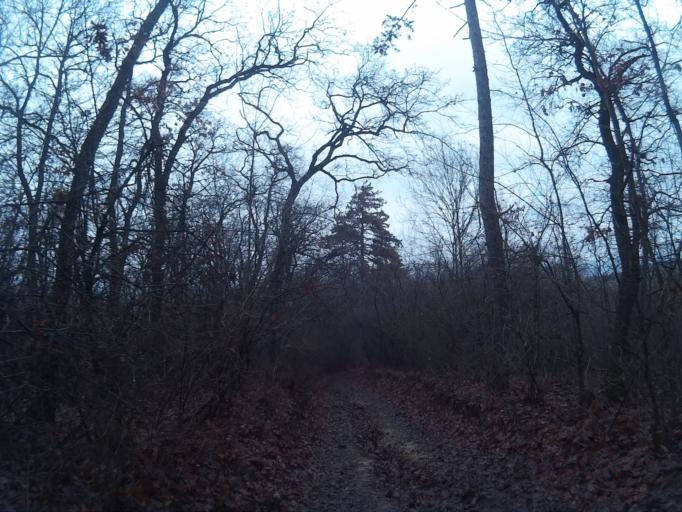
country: HU
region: Komarom-Esztergom
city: Tat
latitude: 47.7257
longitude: 18.6077
